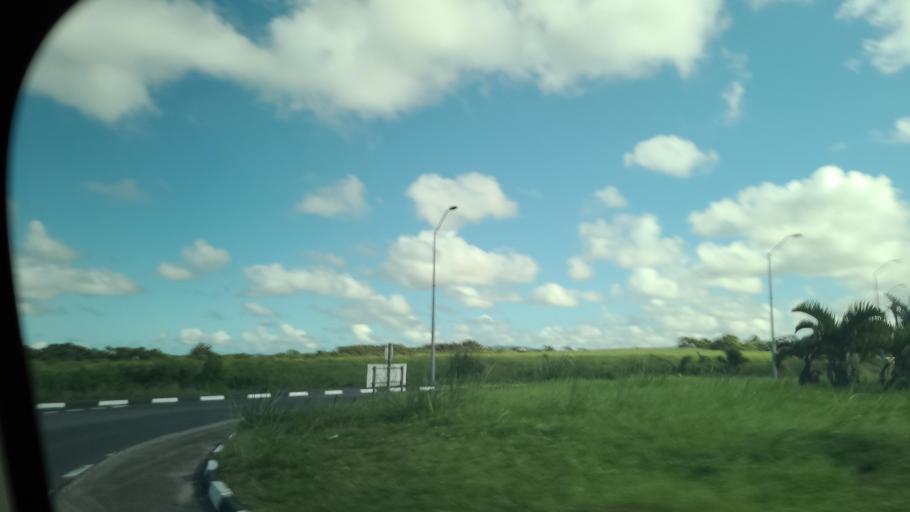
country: MU
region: Flacq
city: Saint Julien
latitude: -20.2364
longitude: 57.6279
